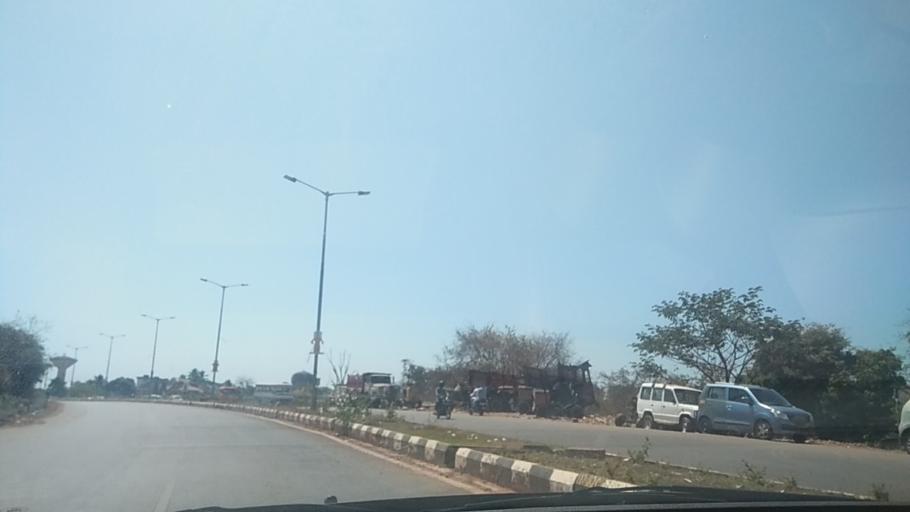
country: IN
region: Goa
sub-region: South Goa
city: Vasco Da Gama
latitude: 15.3881
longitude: 73.8212
